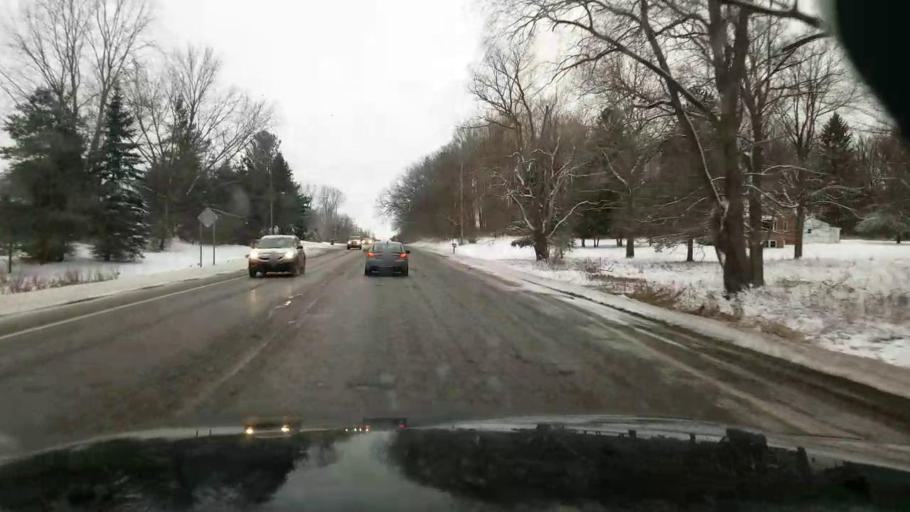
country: US
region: Michigan
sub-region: Jackson County
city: Spring Arbor
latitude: 42.2250
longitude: -84.4944
